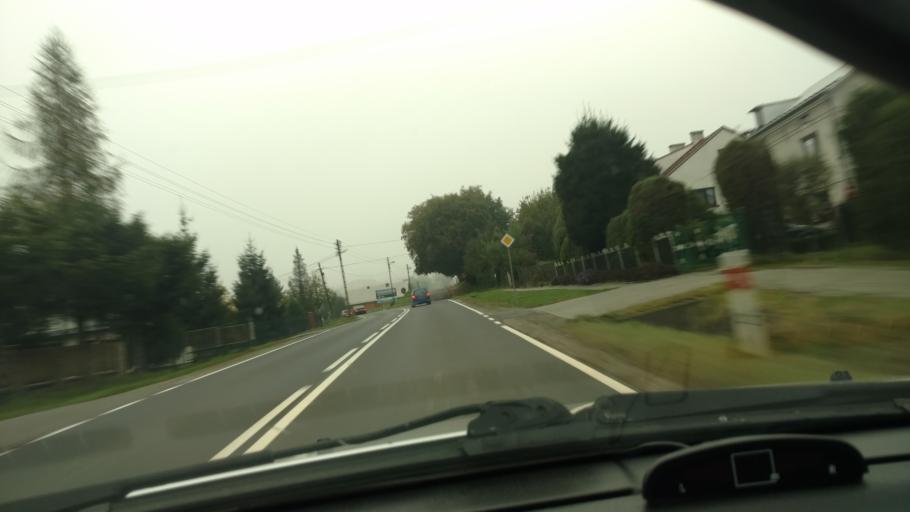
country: PL
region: Subcarpathian Voivodeship
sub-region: Powiat strzyzowski
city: Frysztak
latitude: 49.8434
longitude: 21.6098
